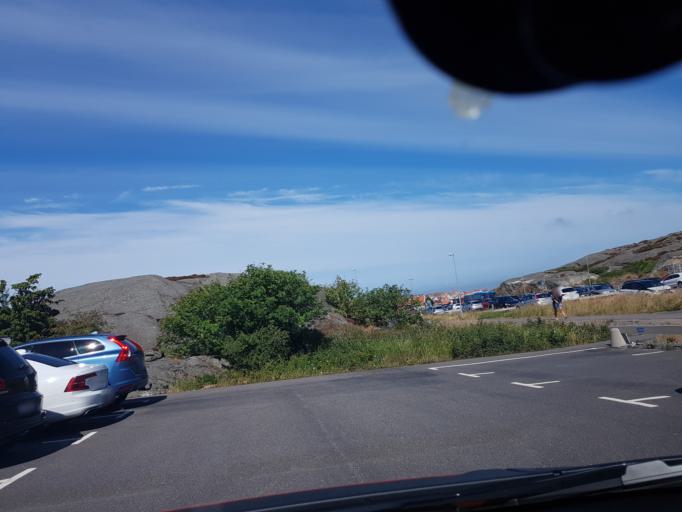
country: SE
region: Vaestra Goetaland
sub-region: Lysekils Kommun
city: Lysekil
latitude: 58.1741
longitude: 11.4178
